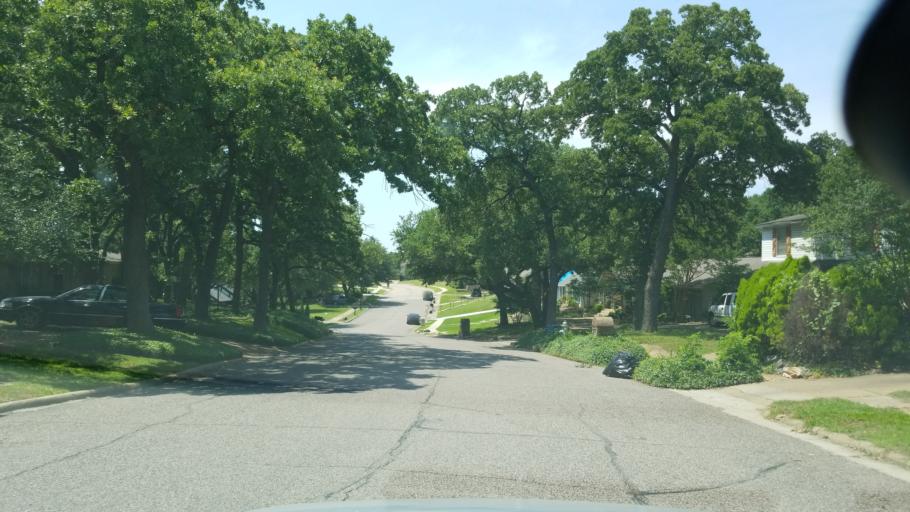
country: US
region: Texas
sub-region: Dallas County
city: Irving
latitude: 32.8509
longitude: -96.9424
